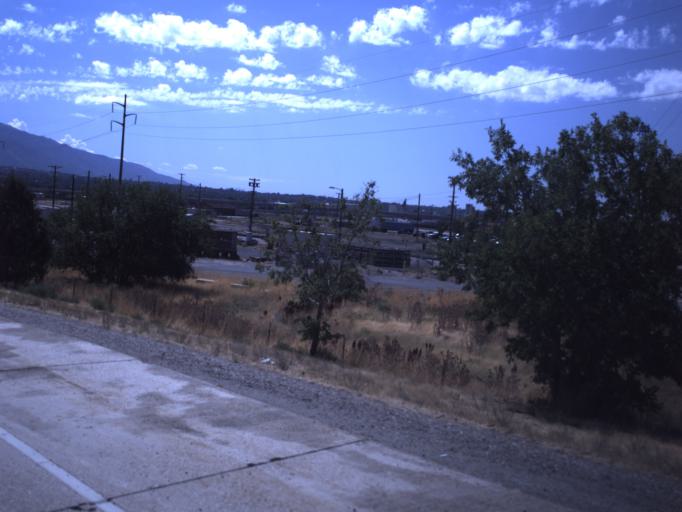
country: US
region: Utah
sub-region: Weber County
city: Ogden
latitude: 41.2300
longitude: -111.9850
